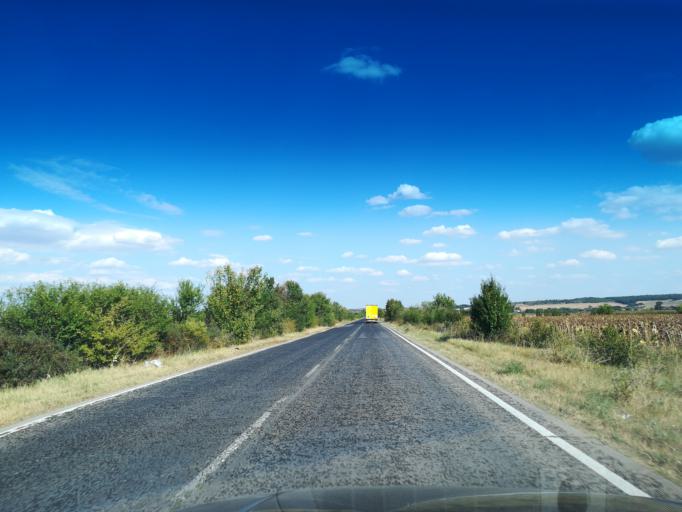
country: BG
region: Khaskovo
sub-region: Obshtina Mineralni Bani
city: Mineralni Bani
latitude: 42.0524
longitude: 25.3235
